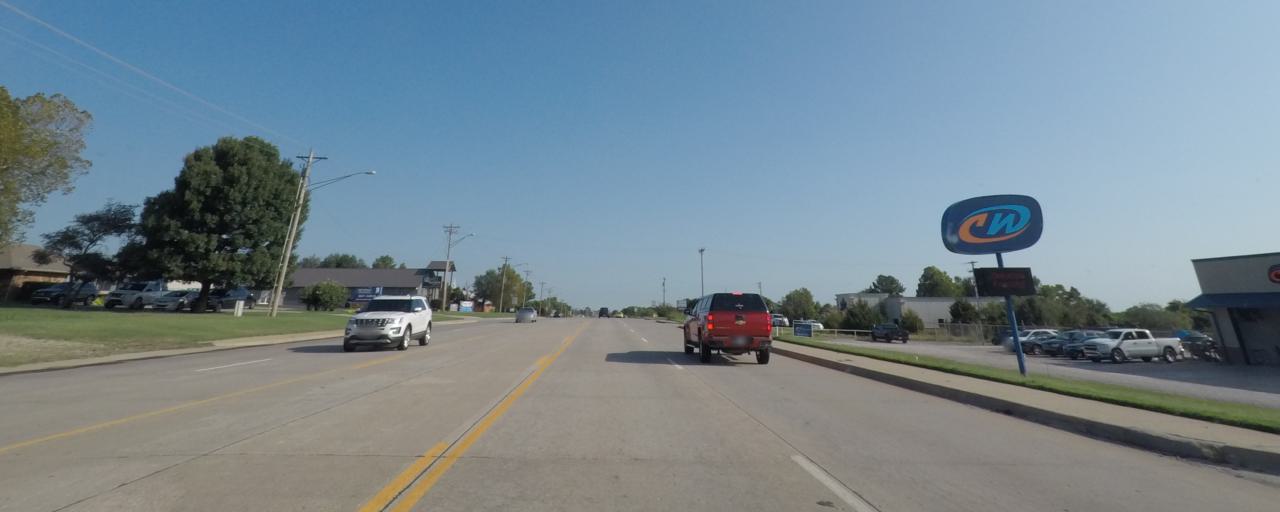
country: US
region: Oklahoma
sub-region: McClain County
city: Newcastle
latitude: 35.2421
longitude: -97.6001
